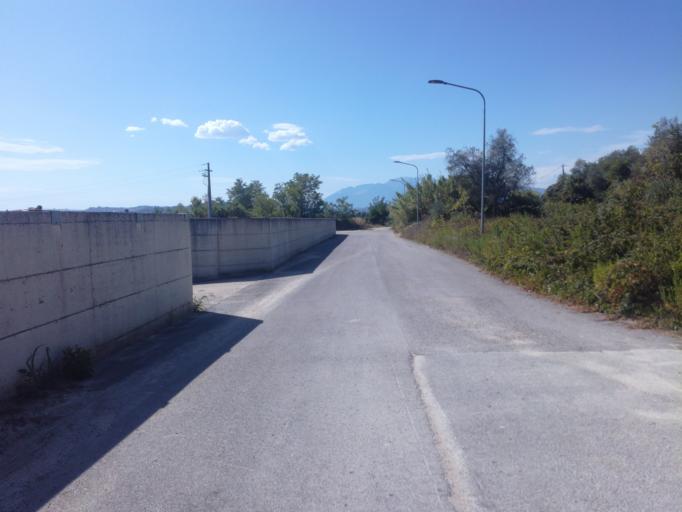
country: IT
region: Abruzzo
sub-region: Provincia di Chieti
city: Miglianico
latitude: 42.3888
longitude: 14.2924
